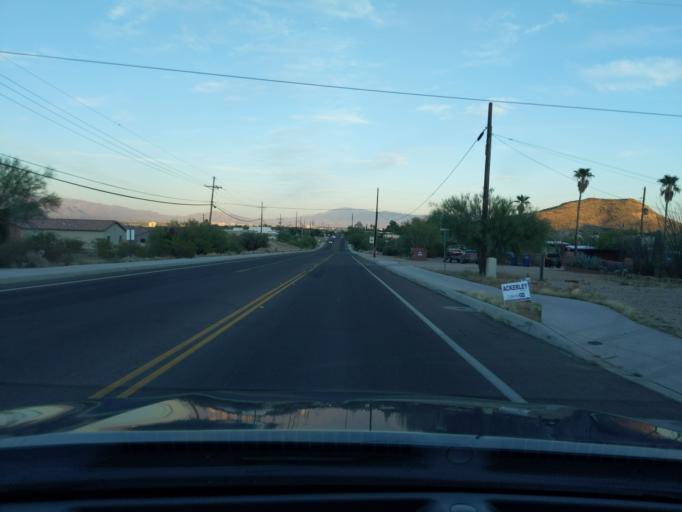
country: US
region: Arizona
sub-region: Pima County
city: Tucson Estates
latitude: 32.2249
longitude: -111.0333
